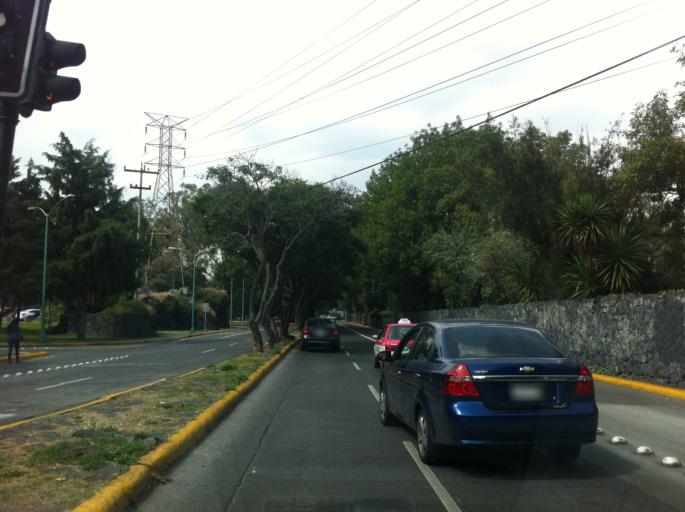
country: MX
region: Mexico City
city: Coyoacan
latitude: 19.3357
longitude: -99.1836
